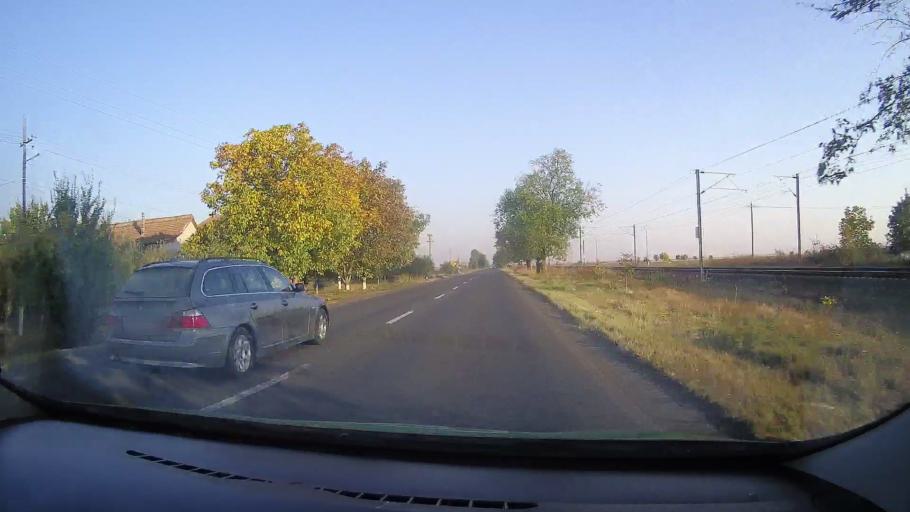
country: RO
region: Arad
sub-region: Comuna Sofronea
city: Sofronea
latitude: 46.2864
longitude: 21.3127
